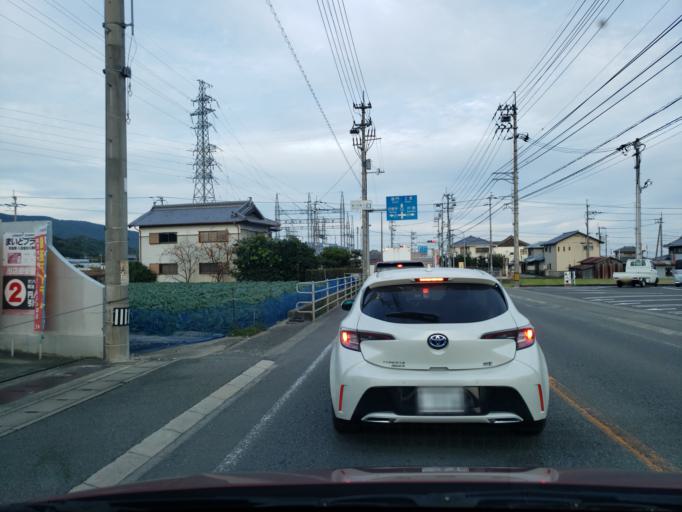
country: JP
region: Tokushima
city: Kamojimacho-jogejima
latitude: 34.0931
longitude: 134.3081
